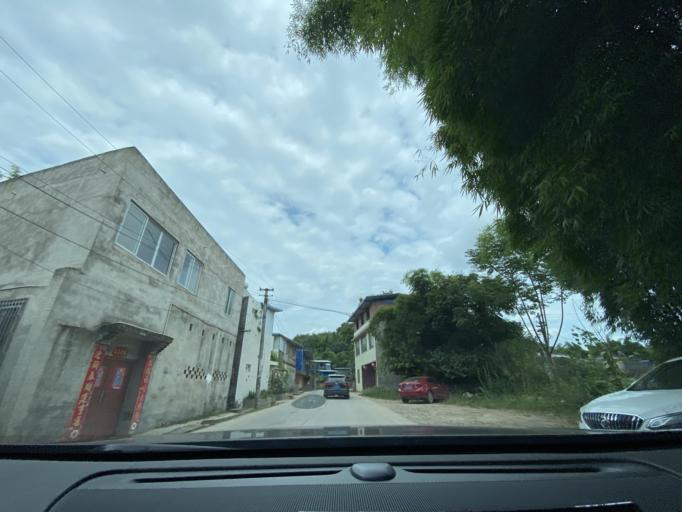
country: CN
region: Sichuan
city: Jiancheng
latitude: 30.4415
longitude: 104.5425
